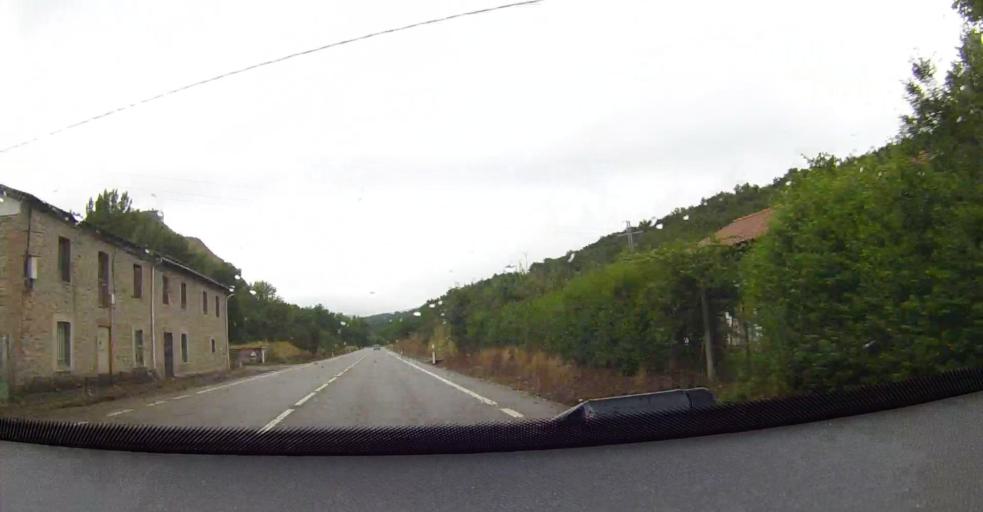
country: ES
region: Castille and Leon
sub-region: Provincia de Leon
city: Cistierna
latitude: 42.8269
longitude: -5.1227
